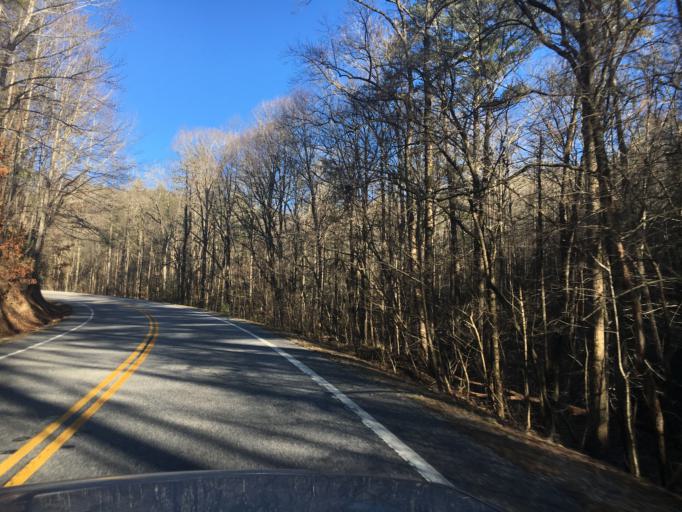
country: US
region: Georgia
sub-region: White County
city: Cleveland
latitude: 34.6645
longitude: -83.8811
